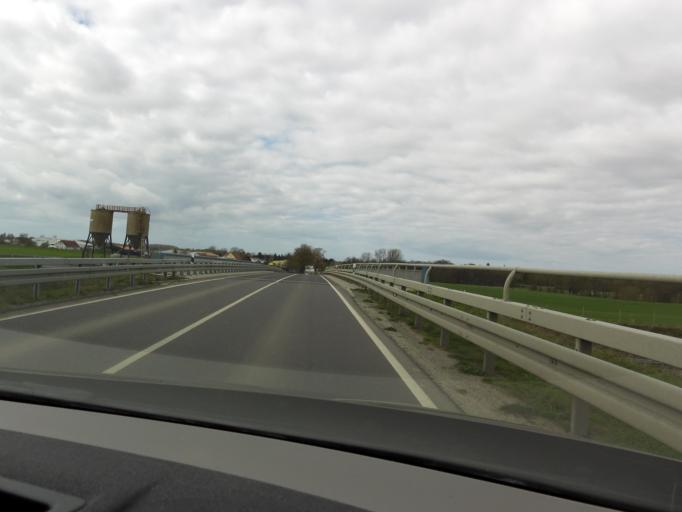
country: DE
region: Mecklenburg-Vorpommern
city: Samtens
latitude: 54.3502
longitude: 13.2993
